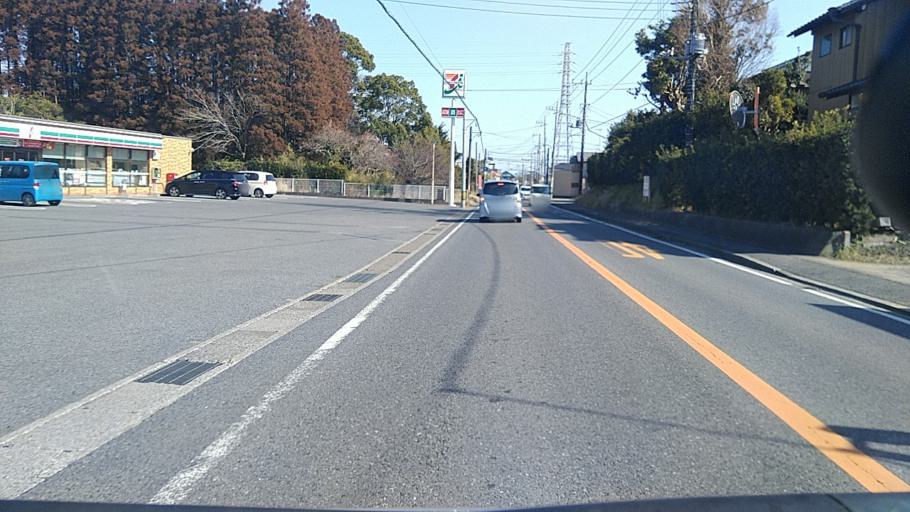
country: JP
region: Chiba
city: Mobara
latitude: 35.4250
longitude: 140.2776
